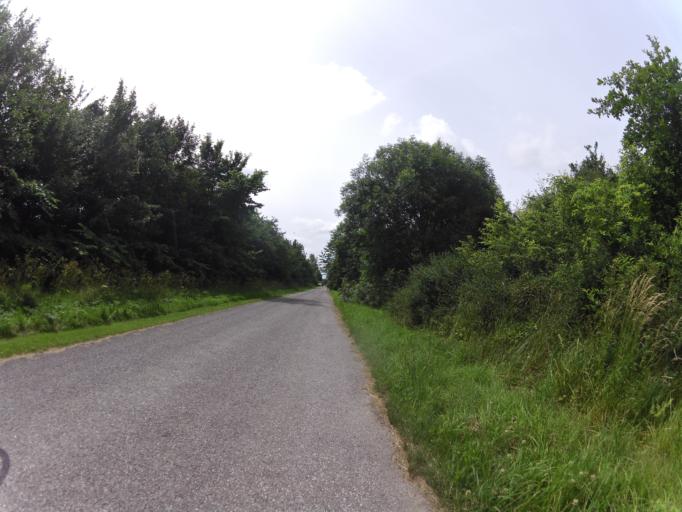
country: DK
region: North Denmark
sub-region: Bronderslev Kommune
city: Dronninglund
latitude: 57.2564
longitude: 10.3053
